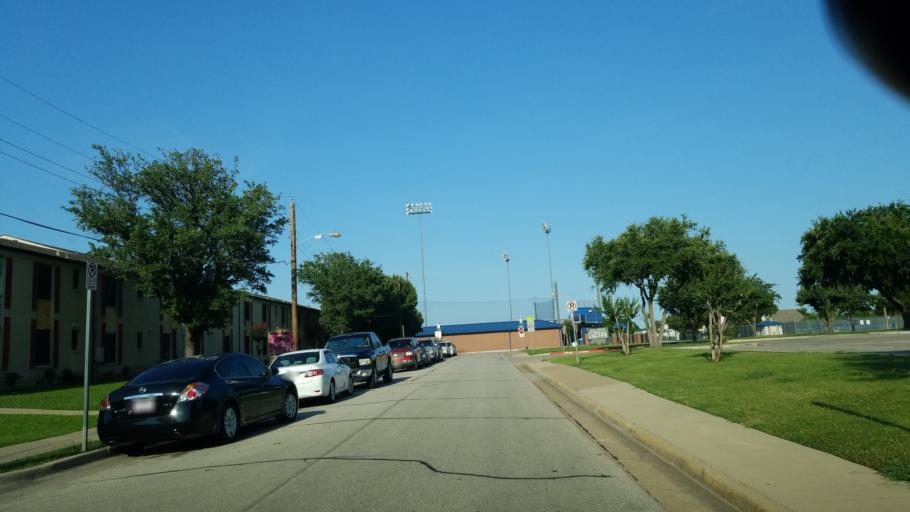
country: US
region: Texas
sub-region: Dallas County
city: Carrollton
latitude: 32.9460
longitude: -96.8942
